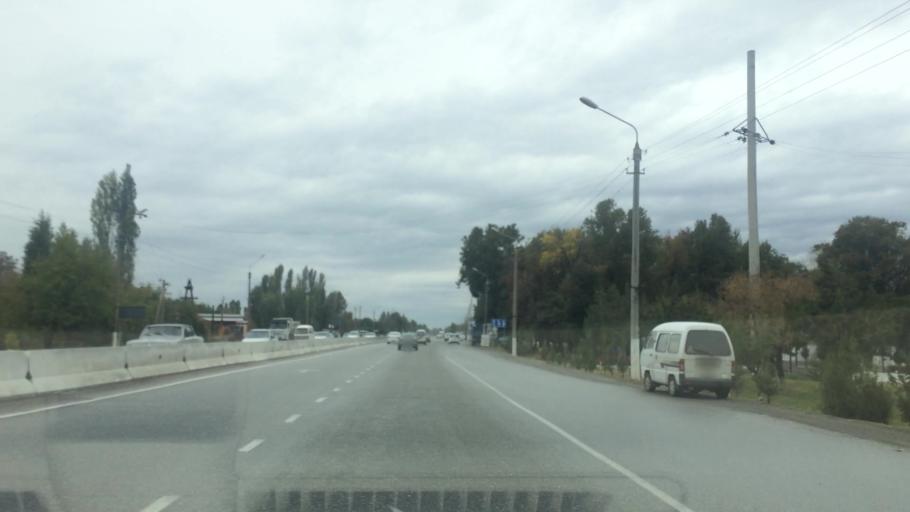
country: UZ
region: Jizzax
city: Jizzax
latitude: 40.0058
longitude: 67.5957
